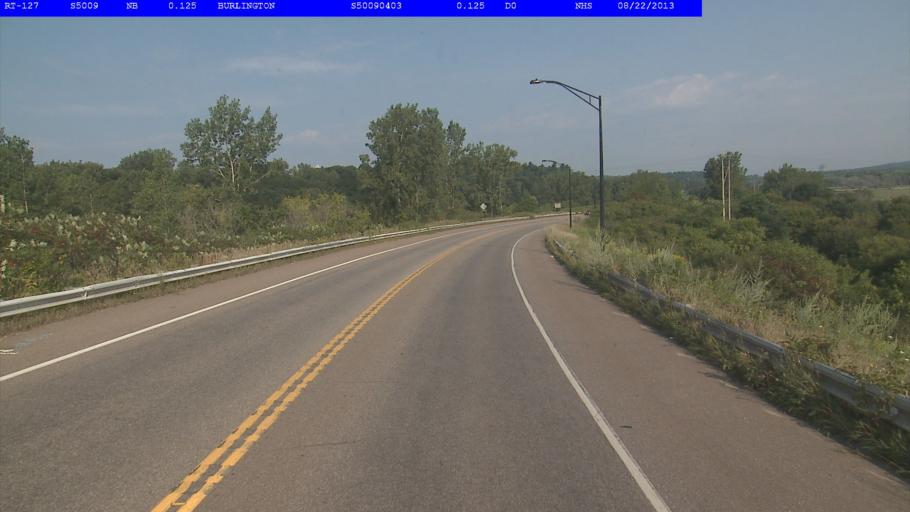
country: US
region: Vermont
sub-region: Chittenden County
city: Burlington
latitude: 44.4887
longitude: -73.2211
